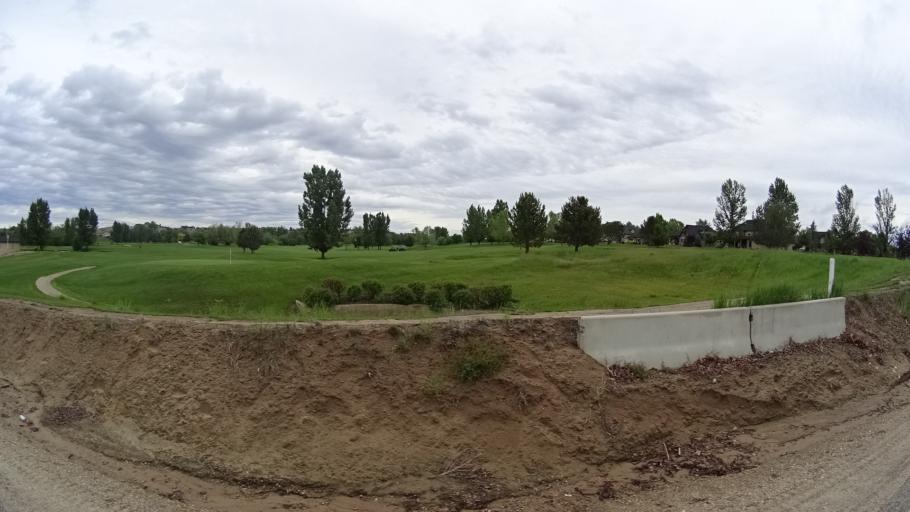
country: US
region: Idaho
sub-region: Ada County
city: Star
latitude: 43.7210
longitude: -116.4649
